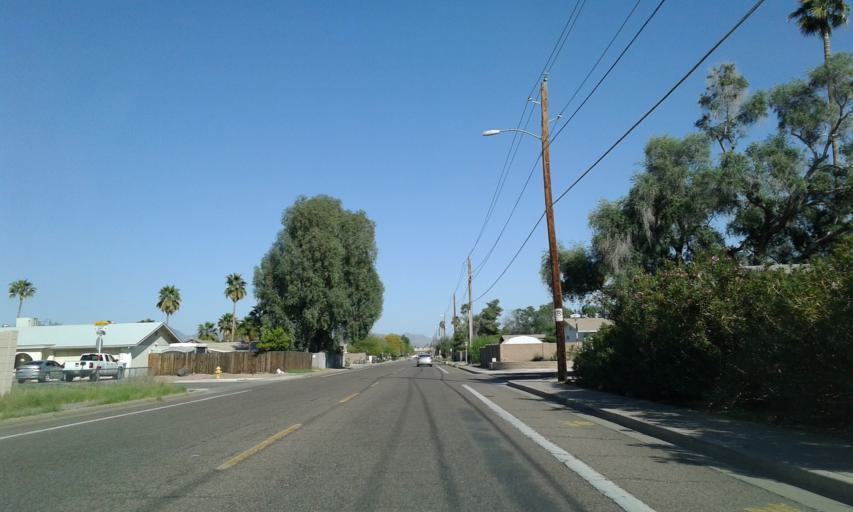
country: US
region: Arizona
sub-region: Maricopa County
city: Paradise Valley
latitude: 33.6042
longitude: -112.0191
